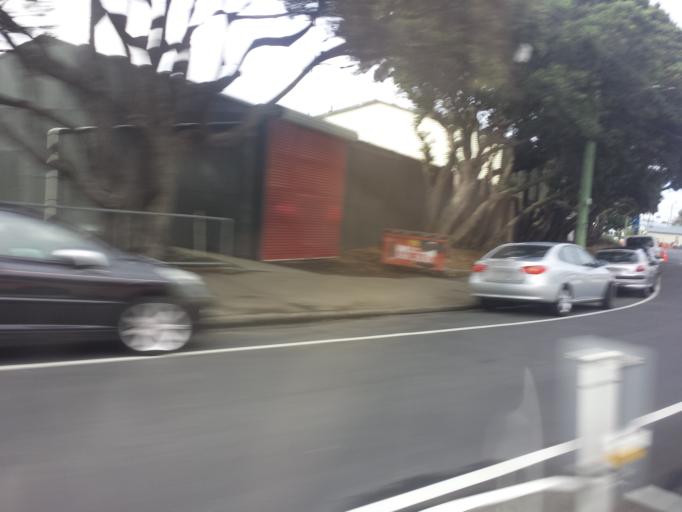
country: NZ
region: Wellington
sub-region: Wellington City
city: Wellington
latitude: -41.3139
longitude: 174.7928
